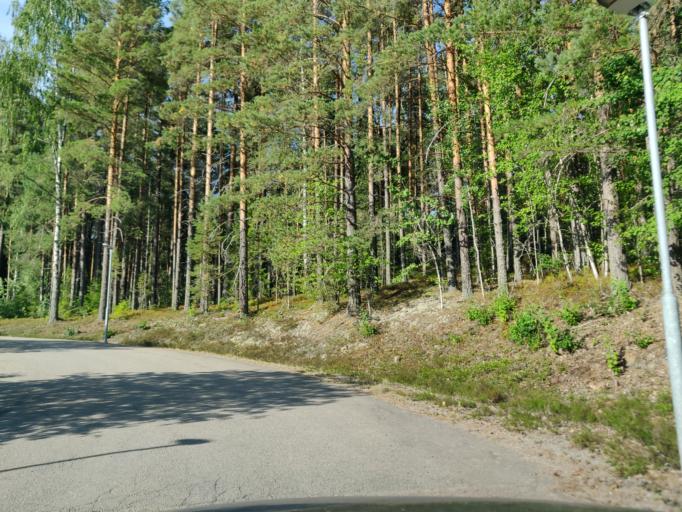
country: SE
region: Vaermland
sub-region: Hagfors Kommun
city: Hagfors
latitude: 60.0329
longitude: 13.7119
